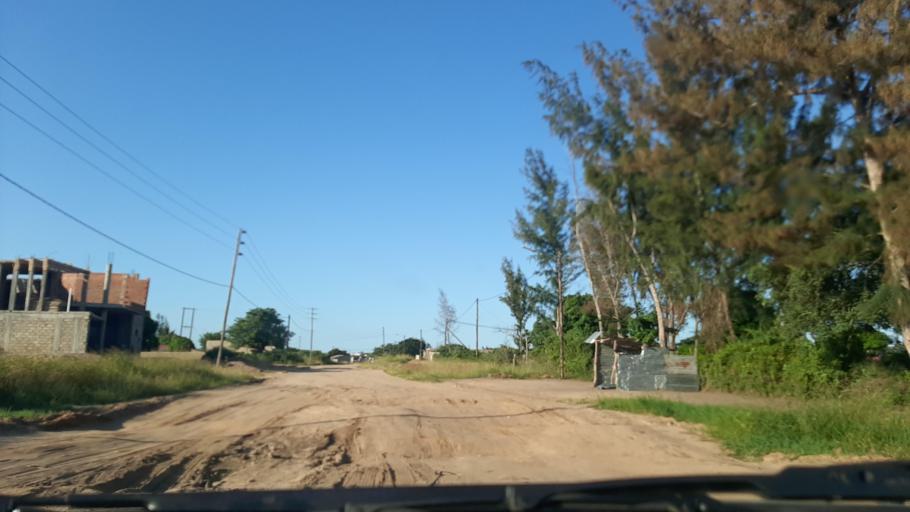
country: MZ
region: Maputo City
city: Maputo
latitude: -25.7602
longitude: 32.5492
